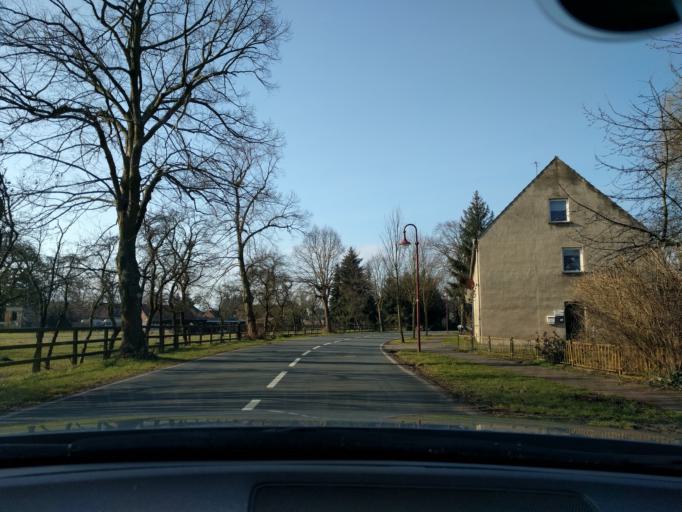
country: DE
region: Saxony-Anhalt
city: Iden
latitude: 52.7547
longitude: 11.9343
